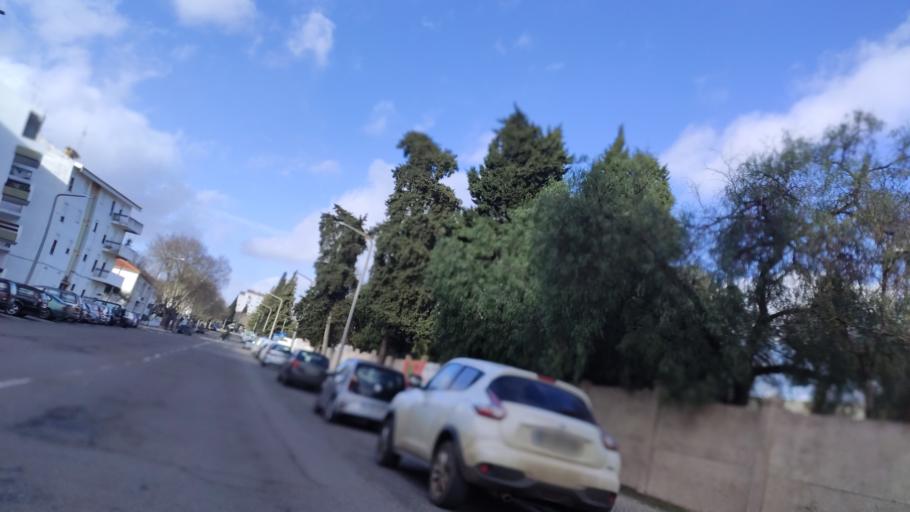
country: PT
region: Beja
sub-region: Beja
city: Beja
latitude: 38.0069
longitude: -7.8624
